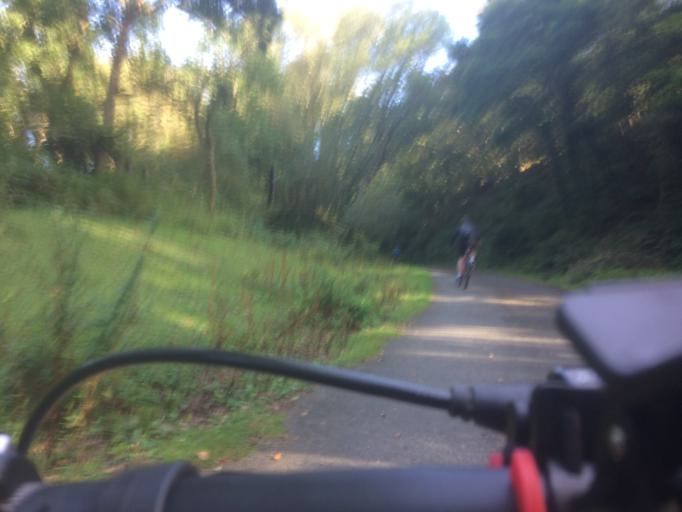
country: GB
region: England
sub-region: Devon
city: Horrabridge
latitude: 50.5133
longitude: -4.1220
